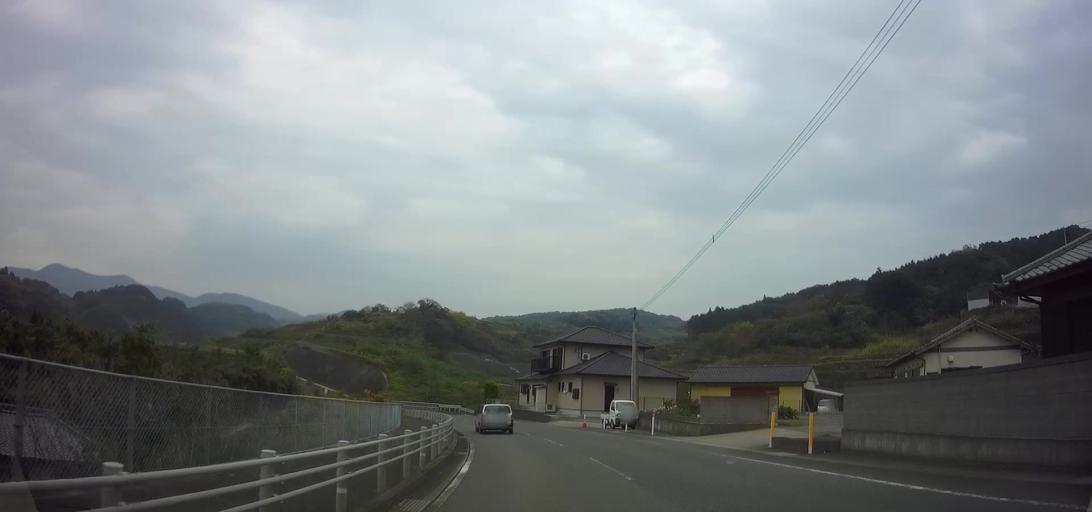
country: JP
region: Nagasaki
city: Shimabara
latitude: 32.7049
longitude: 130.1889
